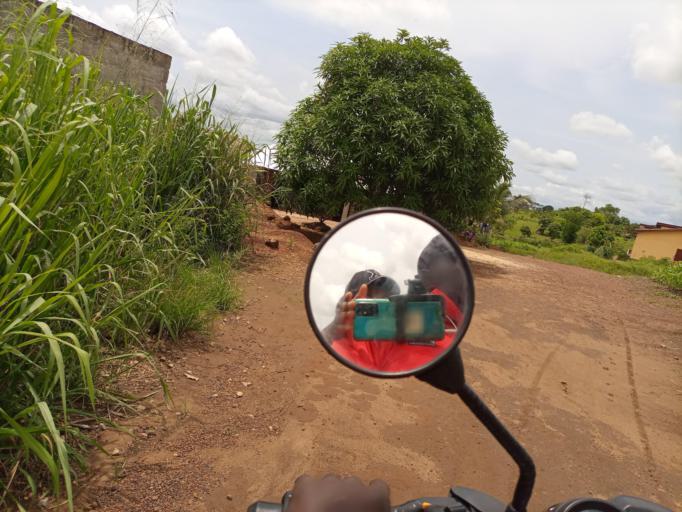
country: SL
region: Southern Province
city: Baoma
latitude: 7.9774
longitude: -11.7196
